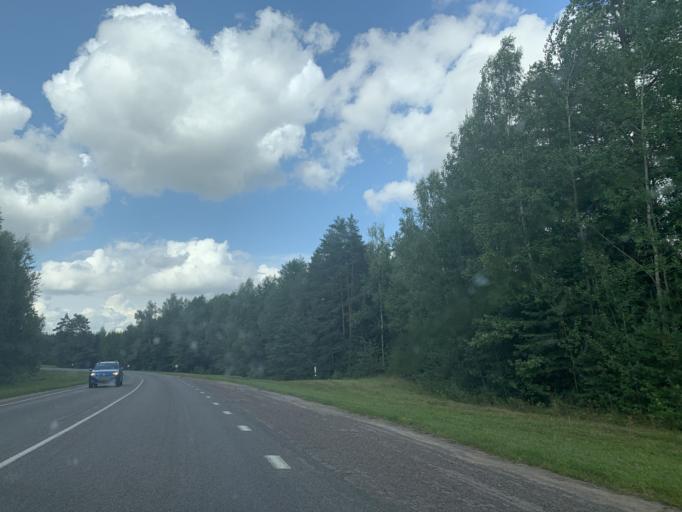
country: BY
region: Minsk
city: Enyerhyetykaw
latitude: 53.5685
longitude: 27.0632
